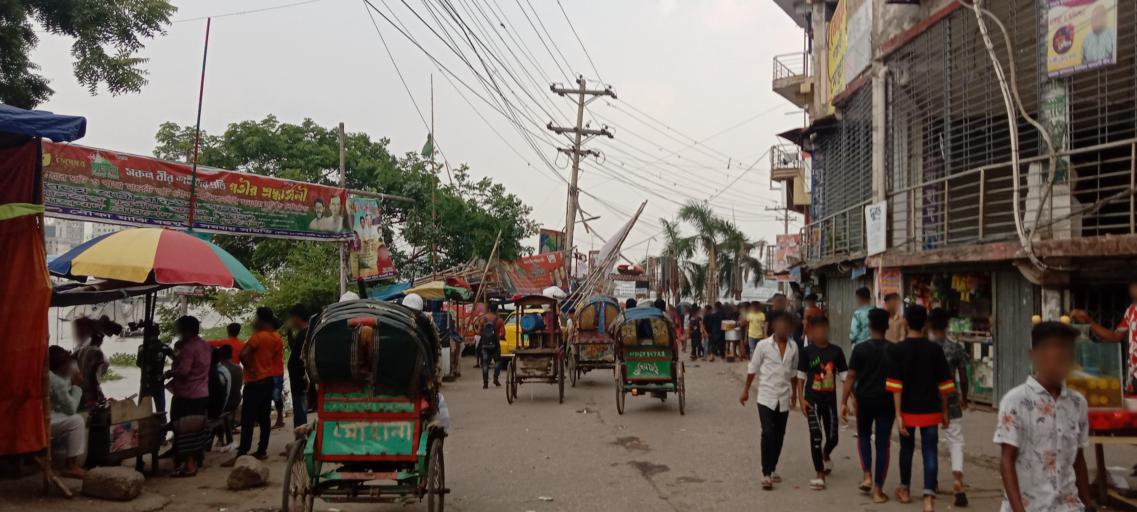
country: BD
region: Dhaka
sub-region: Dhaka
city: Dhaka
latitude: 23.7046
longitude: 90.4061
